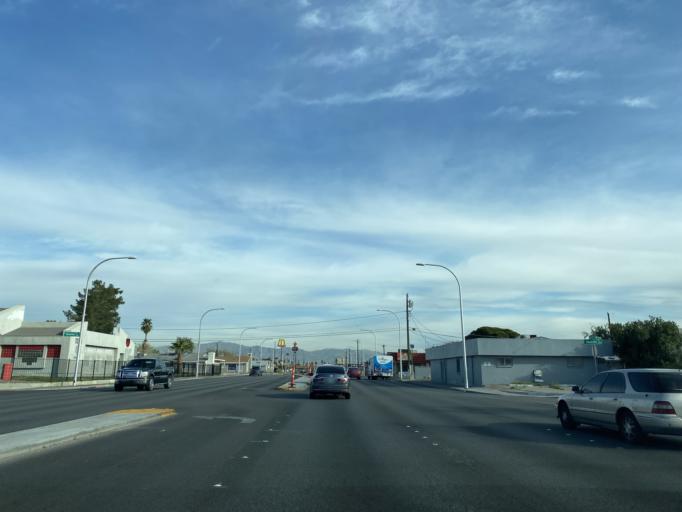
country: US
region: Nevada
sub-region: Clark County
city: Winchester
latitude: 36.1556
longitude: -115.1188
